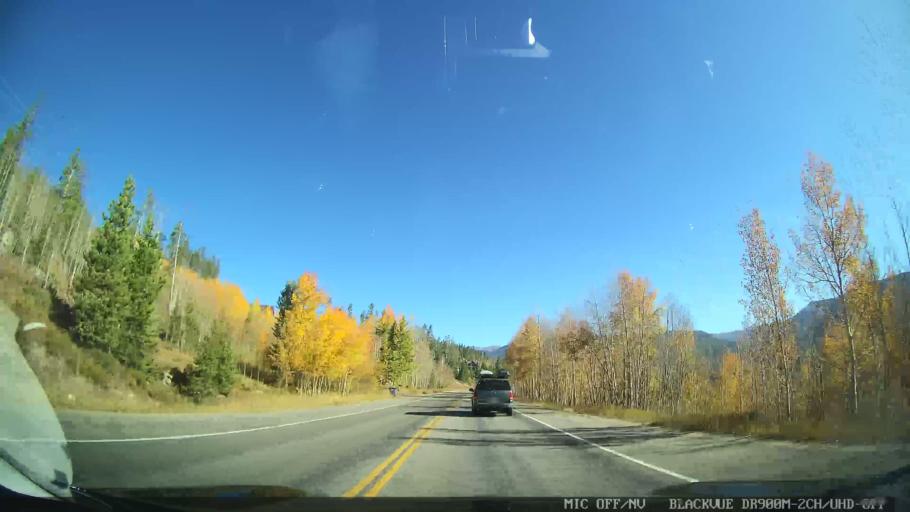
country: US
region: Colorado
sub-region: Grand County
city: Granby
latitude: 40.2427
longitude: -105.8436
